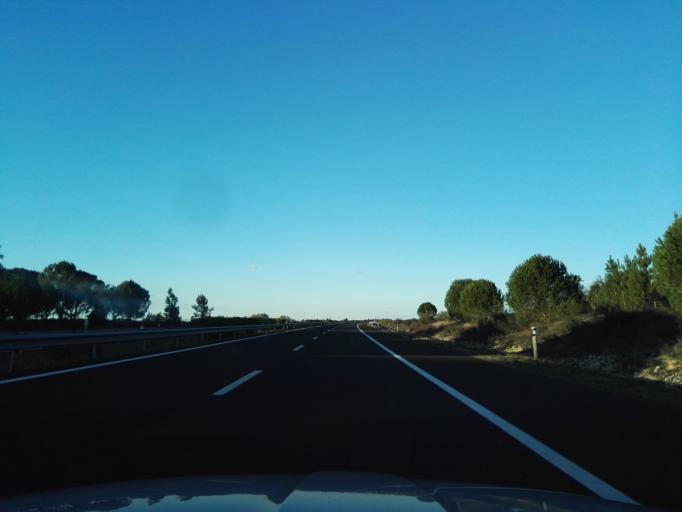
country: PT
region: Santarem
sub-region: Benavente
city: Poceirao
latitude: 38.7505
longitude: -8.6836
